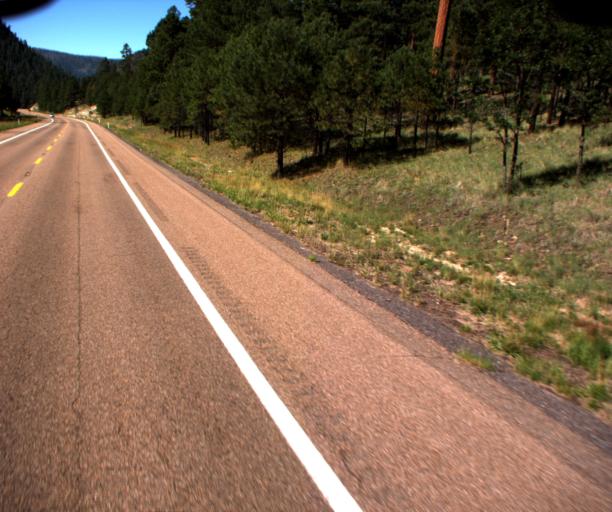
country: US
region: Arizona
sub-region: Apache County
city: Eagar
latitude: 33.8897
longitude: -109.1563
